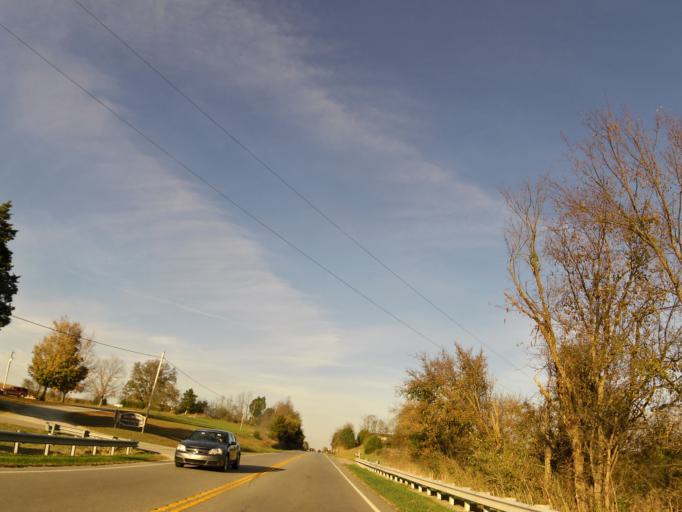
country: US
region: Kentucky
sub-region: Garrard County
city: Lancaster
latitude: 37.5760
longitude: -84.6115
